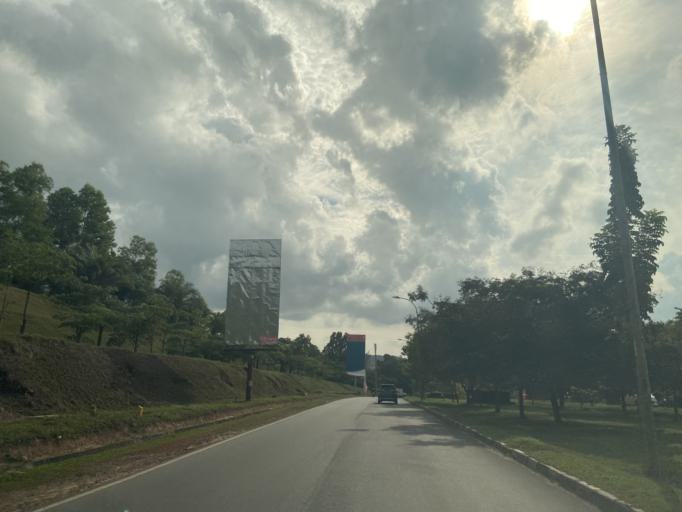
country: SG
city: Singapore
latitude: 1.0986
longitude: 104.0512
